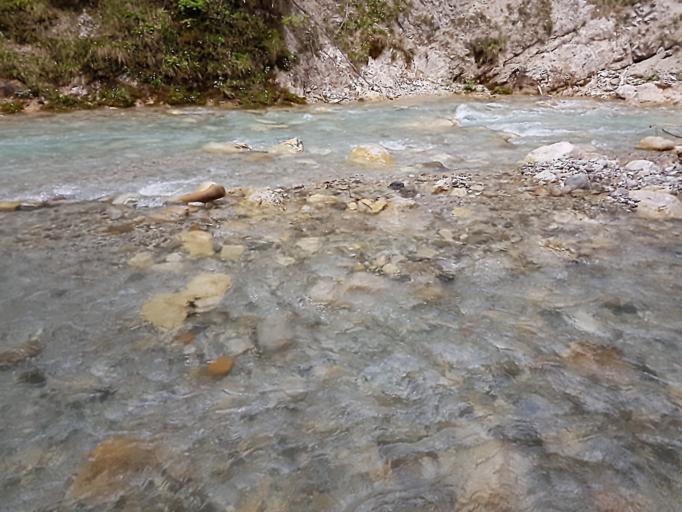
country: AT
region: Carinthia
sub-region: Politischer Bezirk Klagenfurt Land
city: Ferlach
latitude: 46.4885
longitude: 14.2785
